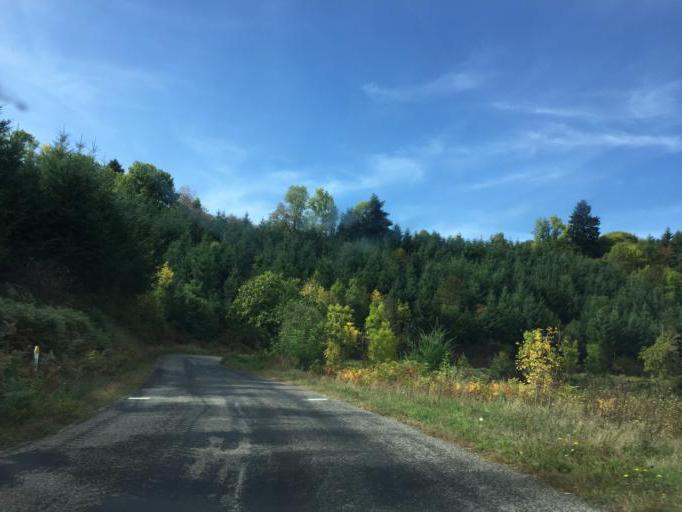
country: FR
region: Rhone-Alpes
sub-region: Departement du Rhone
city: Grandris
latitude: 46.0469
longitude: 4.4727
